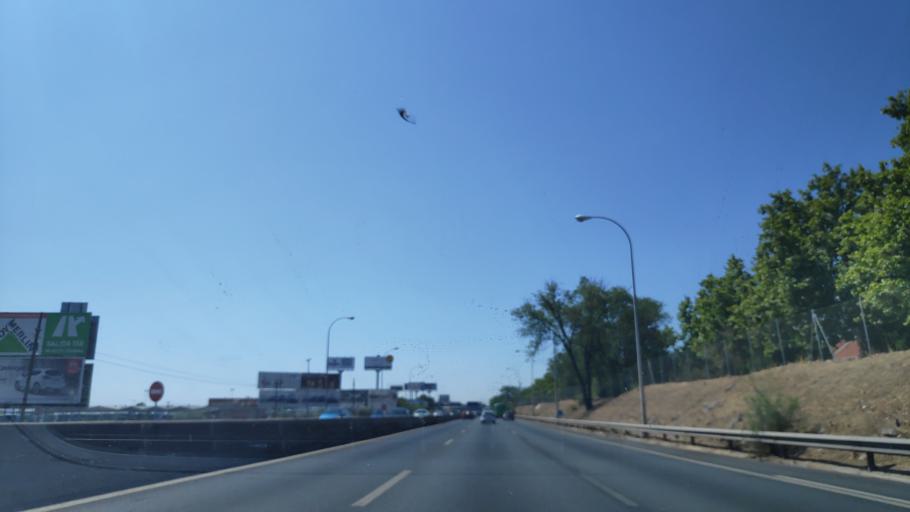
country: ES
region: Madrid
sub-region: Provincia de Madrid
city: Getafe
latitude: 40.2911
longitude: -3.7407
